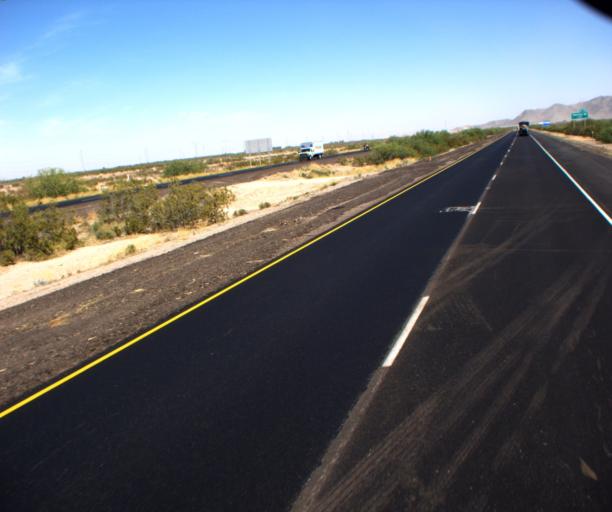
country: US
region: Arizona
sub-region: Pinal County
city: Casa Grande
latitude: 32.8279
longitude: -111.7928
